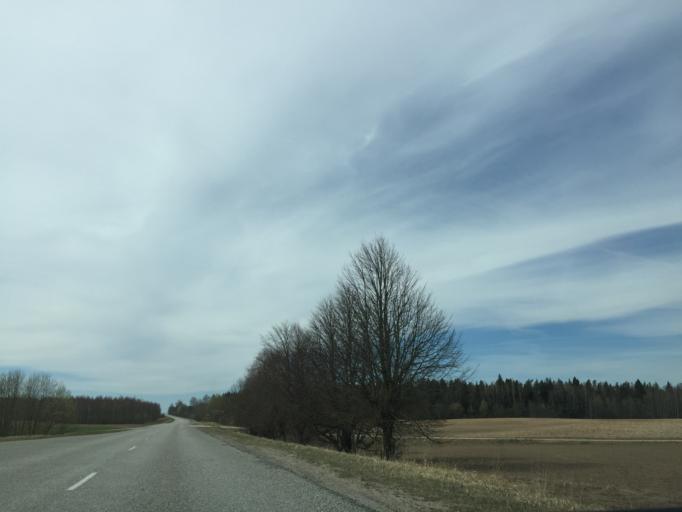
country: LV
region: Valkas Rajons
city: Valka
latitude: 57.7805
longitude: 25.9511
